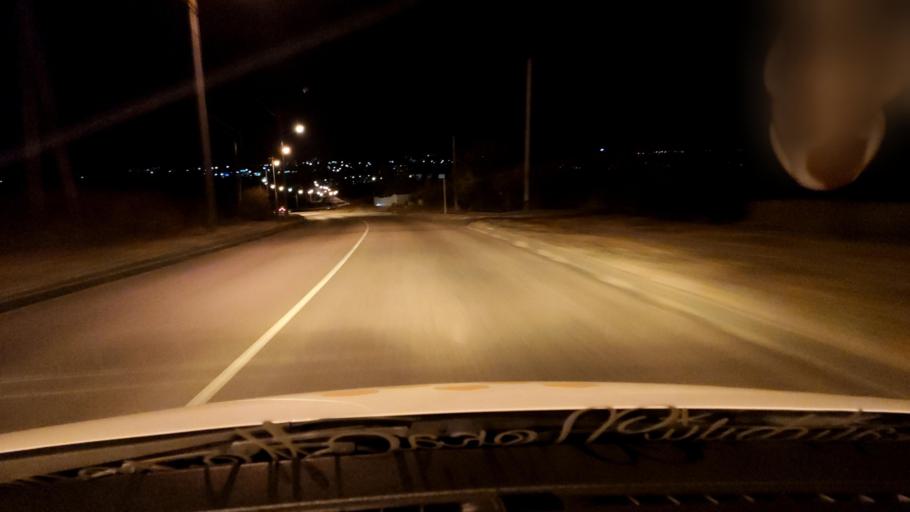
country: RU
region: Voronezj
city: Semiluki
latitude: 51.6693
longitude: 39.0373
